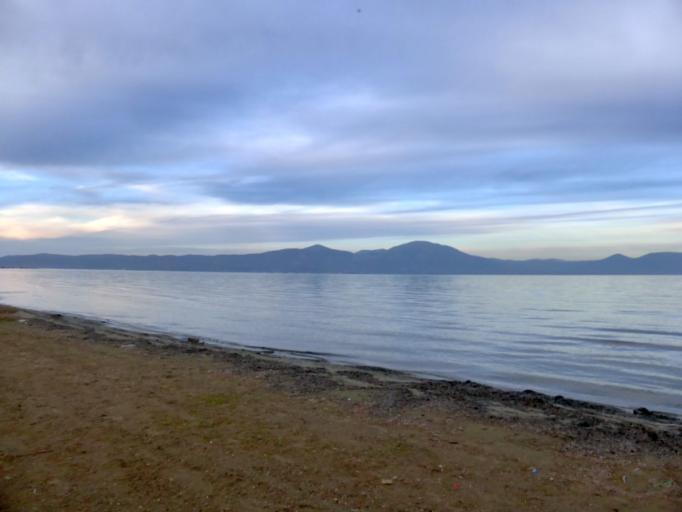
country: GR
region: Attica
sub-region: Nomarchia Anatolikis Attikis
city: Skala Oropou
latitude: 38.3230
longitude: 23.7825
